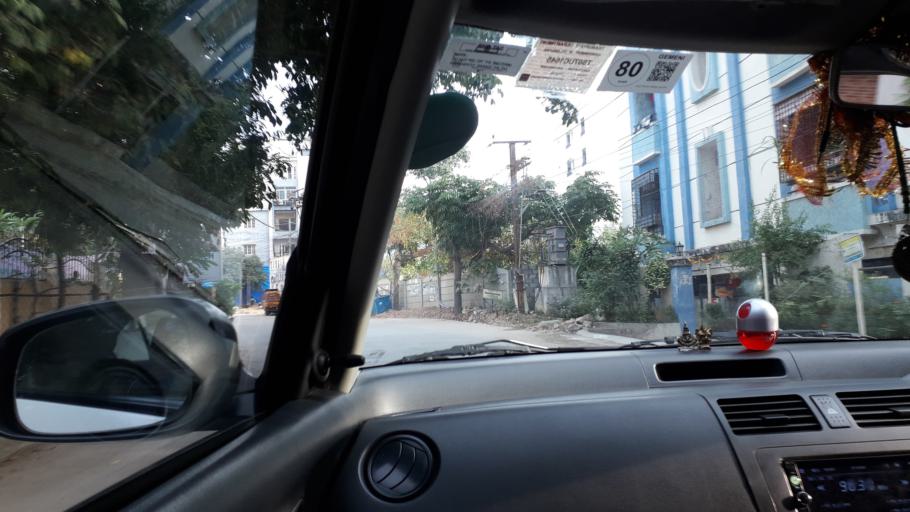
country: IN
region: Telangana
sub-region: Hyderabad
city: Hyderabad
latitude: 17.3948
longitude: 78.3772
